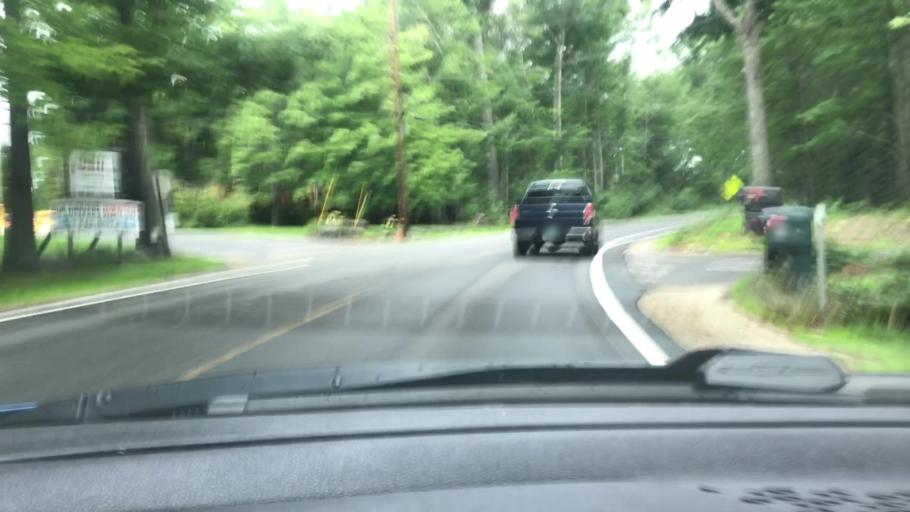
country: US
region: New Hampshire
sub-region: Merrimack County
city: Epsom
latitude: 43.2160
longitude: -71.2867
